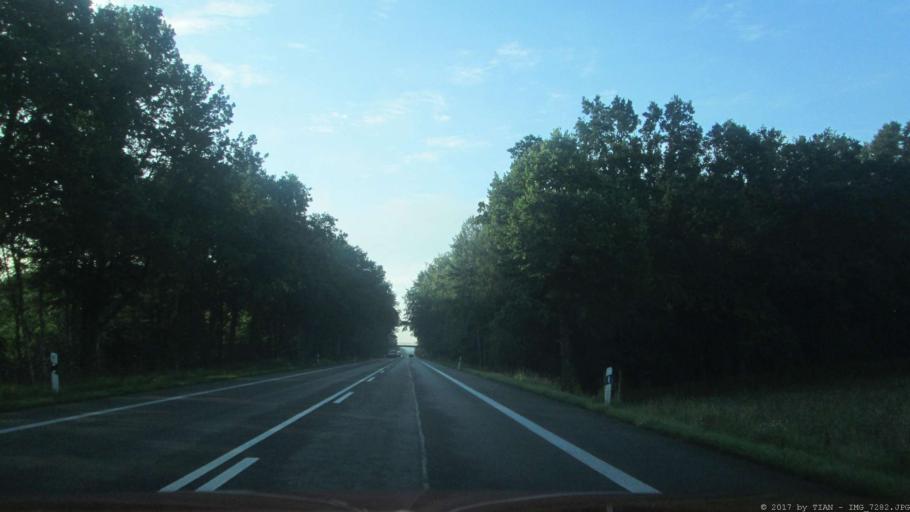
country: DE
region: Lower Saxony
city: Bienenbuttel
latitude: 53.1442
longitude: 10.4727
